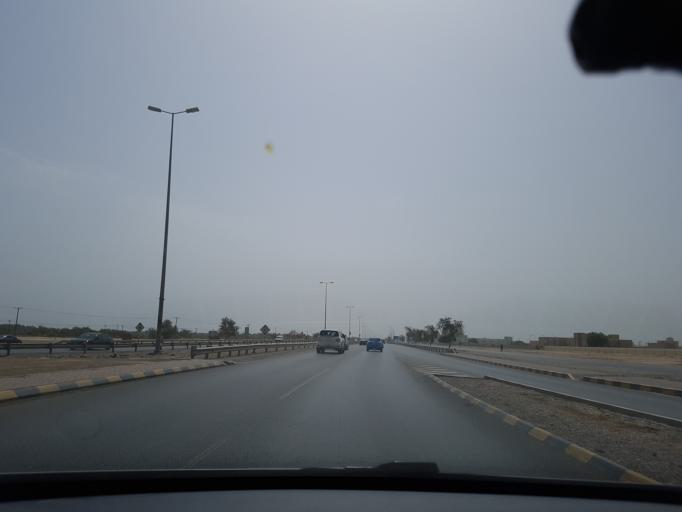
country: OM
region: Al Batinah
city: As Suwayq
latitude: 23.8238
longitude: 57.4249
